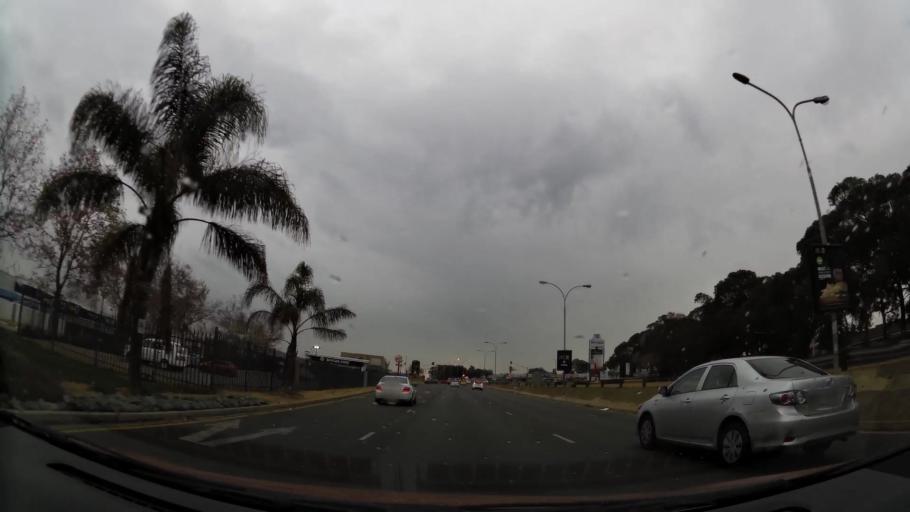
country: ZA
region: Gauteng
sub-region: City of Johannesburg Metropolitan Municipality
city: Roodepoort
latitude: -26.1336
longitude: 27.8572
